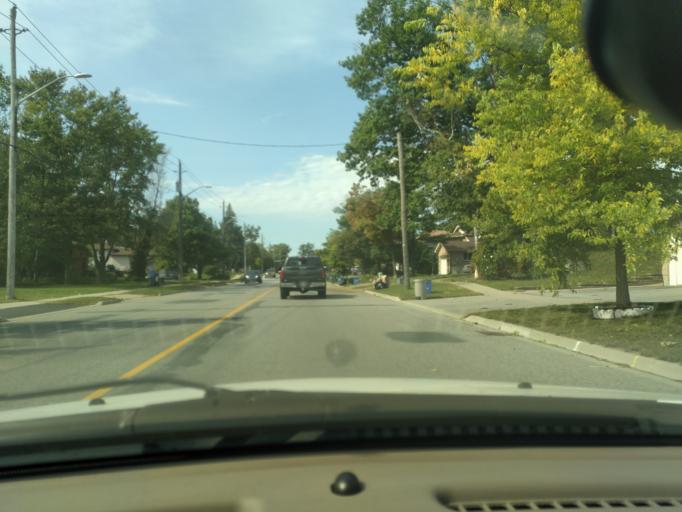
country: CA
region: Ontario
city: Barrie
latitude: 44.3821
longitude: -79.7213
